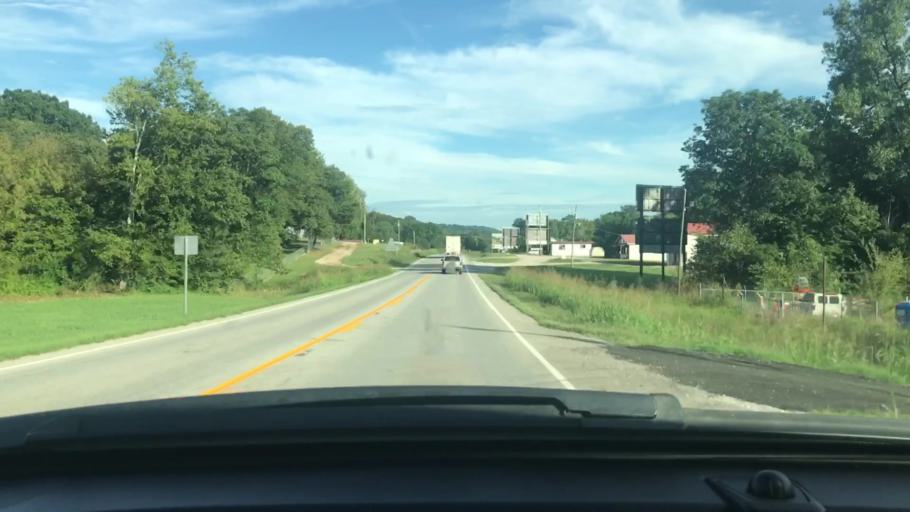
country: US
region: Arkansas
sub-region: Sharp County
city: Cherokee Village
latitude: 36.3018
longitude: -91.4441
